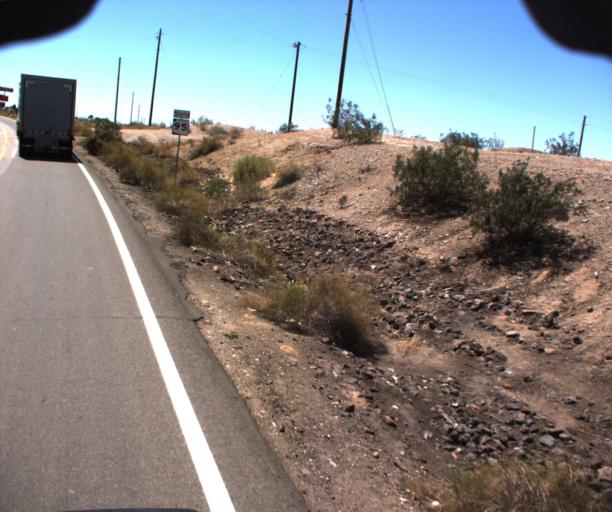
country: US
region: Arizona
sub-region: Mohave County
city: Desert Hills
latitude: 34.7281
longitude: -114.3166
